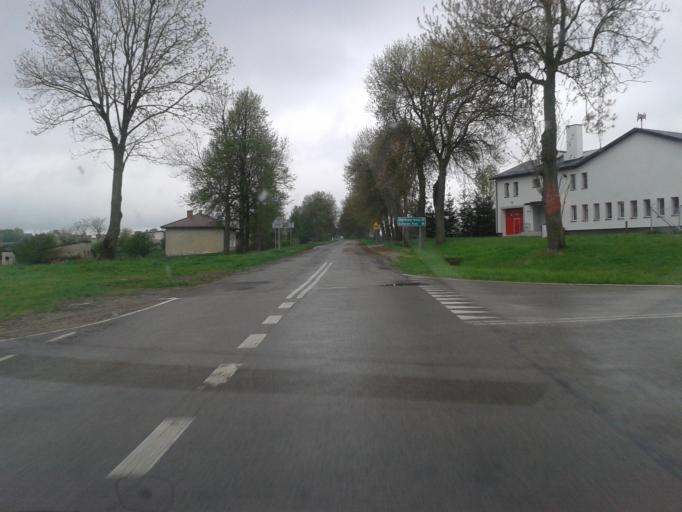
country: PL
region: Lublin Voivodeship
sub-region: Powiat tomaszowski
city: Telatyn
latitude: 50.5235
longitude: 23.9134
